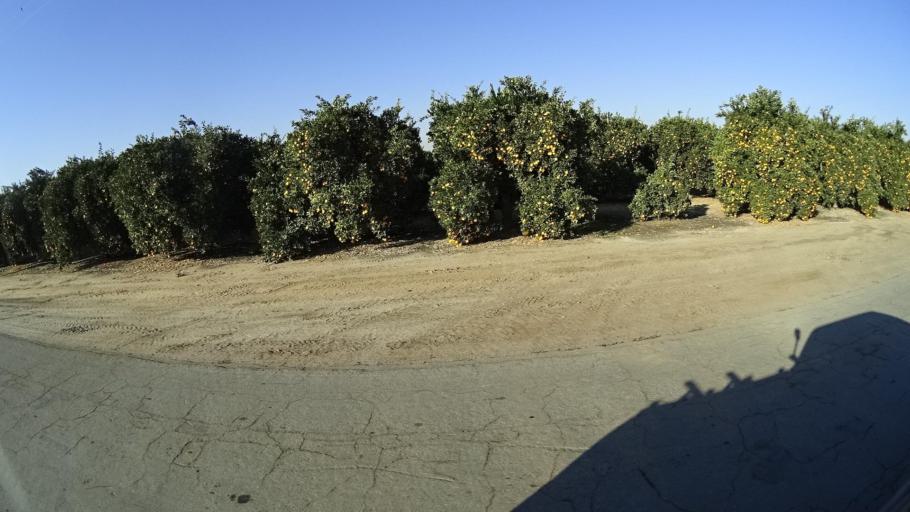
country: US
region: California
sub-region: Tulare County
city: Richgrove
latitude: 35.7690
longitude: -119.1499
